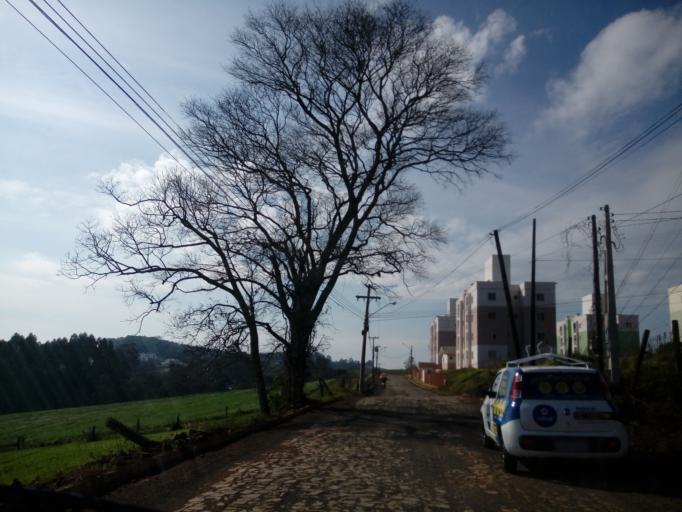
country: BR
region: Santa Catarina
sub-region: Chapeco
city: Chapeco
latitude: -27.1066
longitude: -52.5809
